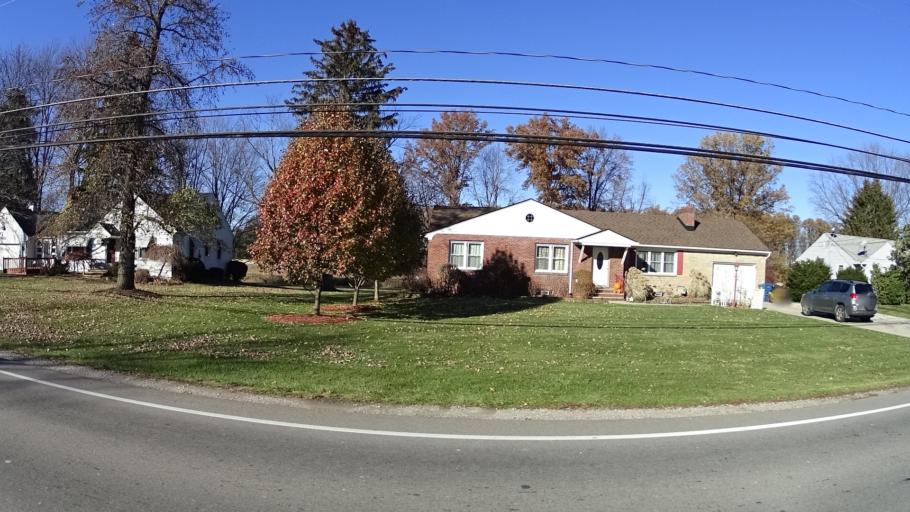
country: US
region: Ohio
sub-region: Lorain County
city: Elyria
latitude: 41.3245
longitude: -82.0869
